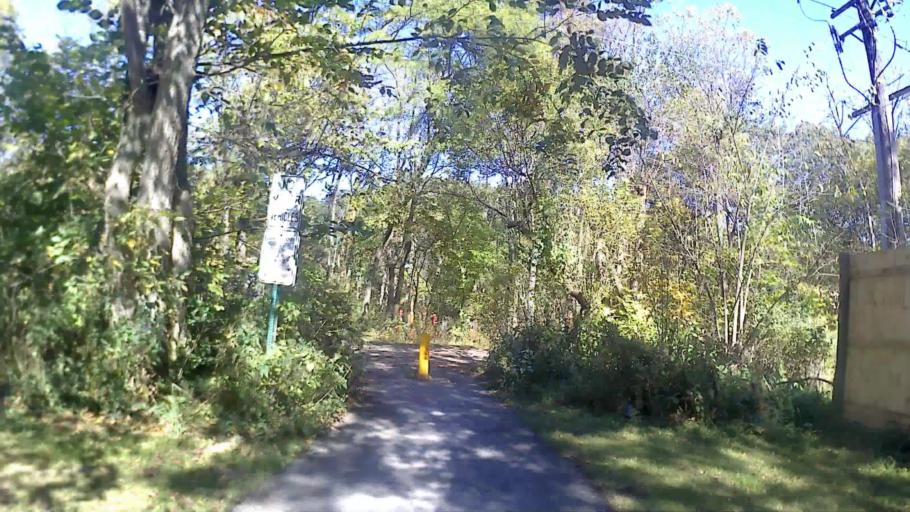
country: US
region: Illinois
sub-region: DuPage County
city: Glen Ellyn
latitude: 41.8797
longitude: -88.0500
